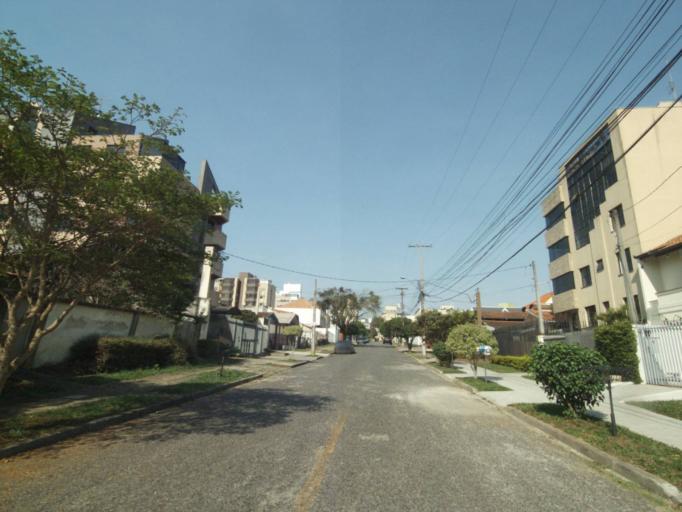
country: BR
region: Parana
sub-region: Curitiba
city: Curitiba
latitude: -25.4628
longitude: -49.2956
